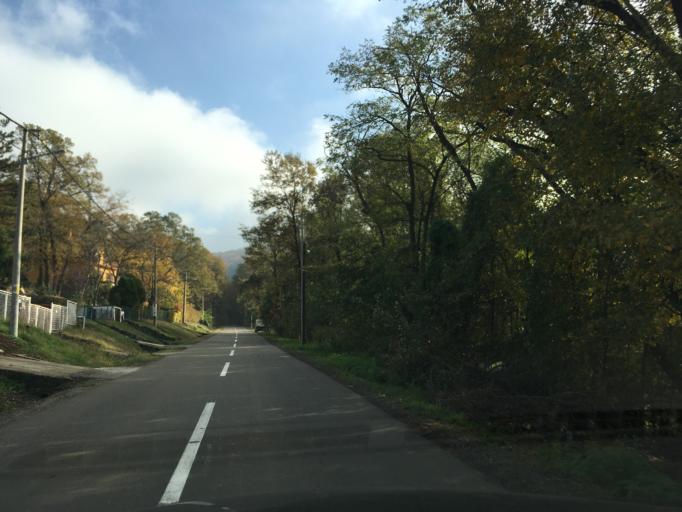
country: RS
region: Central Serbia
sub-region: Belgrade
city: Sopot
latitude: 44.4771
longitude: 20.5645
